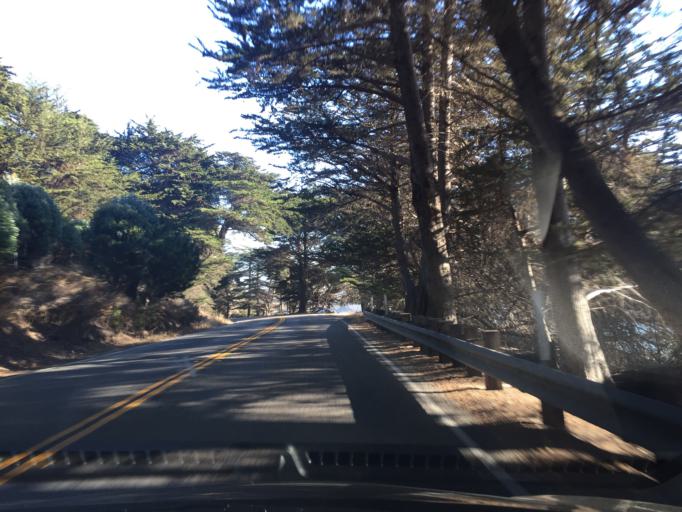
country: US
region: California
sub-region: San Luis Obispo County
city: Cambria
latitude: 35.7767
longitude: -121.3278
